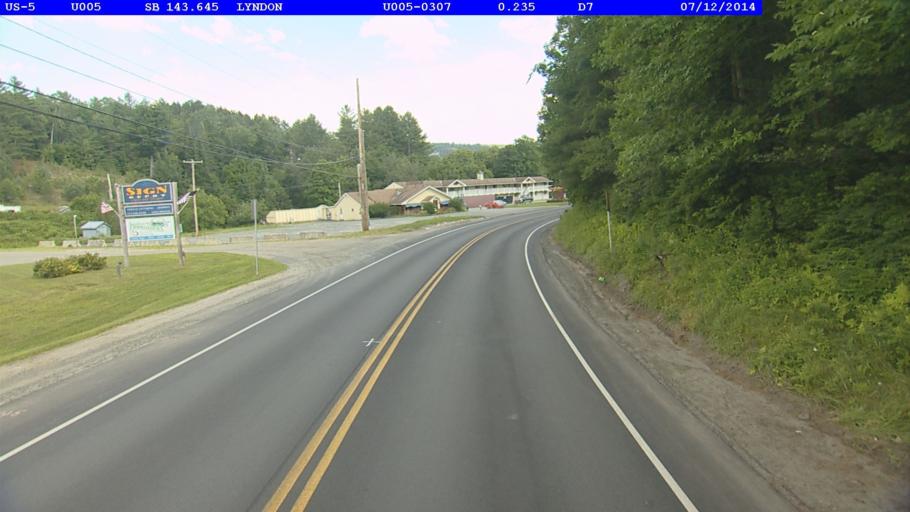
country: US
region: Vermont
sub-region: Caledonia County
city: Lyndon
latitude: 44.5017
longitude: -72.0048
